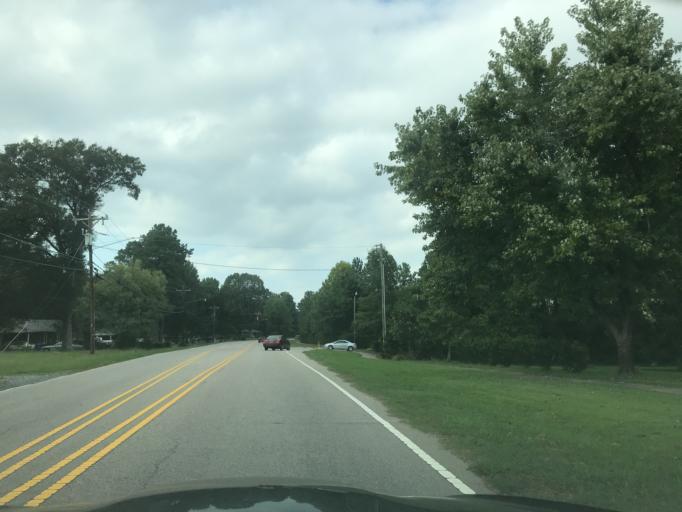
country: US
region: North Carolina
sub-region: Durham County
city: Durham
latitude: 35.9132
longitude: -78.9172
